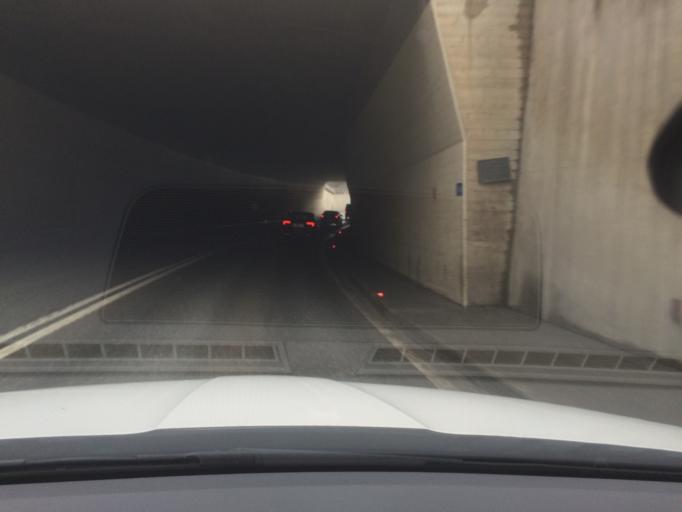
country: AT
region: Tyrol
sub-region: Politischer Bezirk Kitzbuhel
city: Kirchberg in Tirol
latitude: 47.4514
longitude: 12.3222
